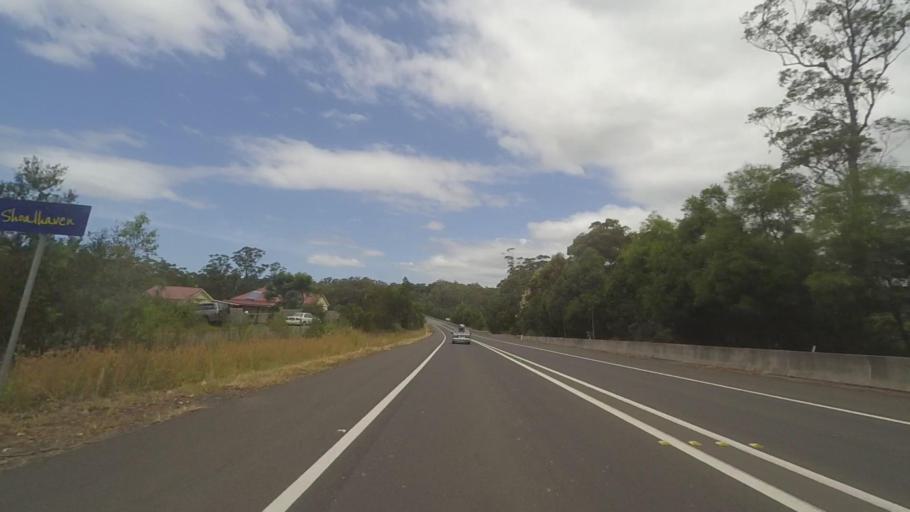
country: AU
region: New South Wales
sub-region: Shoalhaven Shire
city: Milton
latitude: -35.2129
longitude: 150.4357
